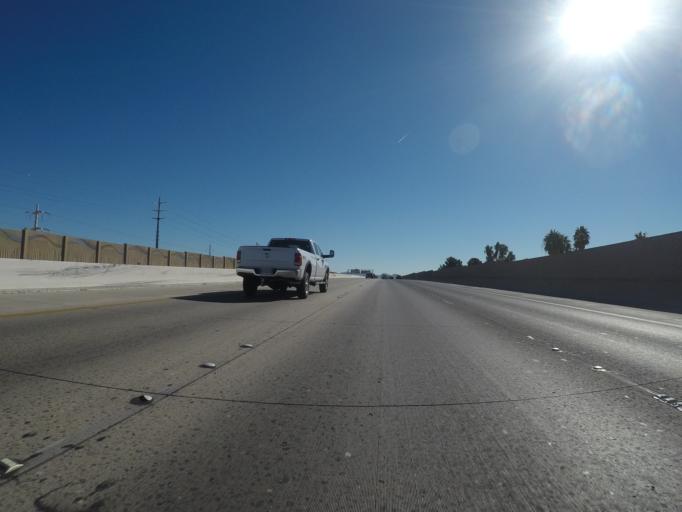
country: US
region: Nevada
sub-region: Clark County
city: Whitney
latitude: 36.0935
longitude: -115.0757
